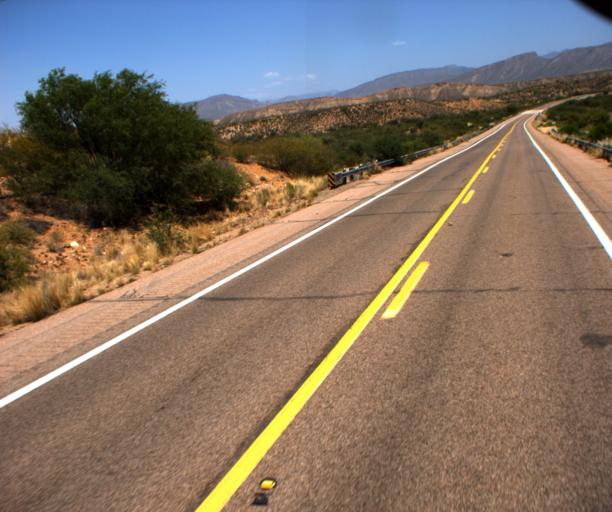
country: US
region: Arizona
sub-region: Gila County
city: Miami
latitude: 33.6140
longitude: -111.0251
